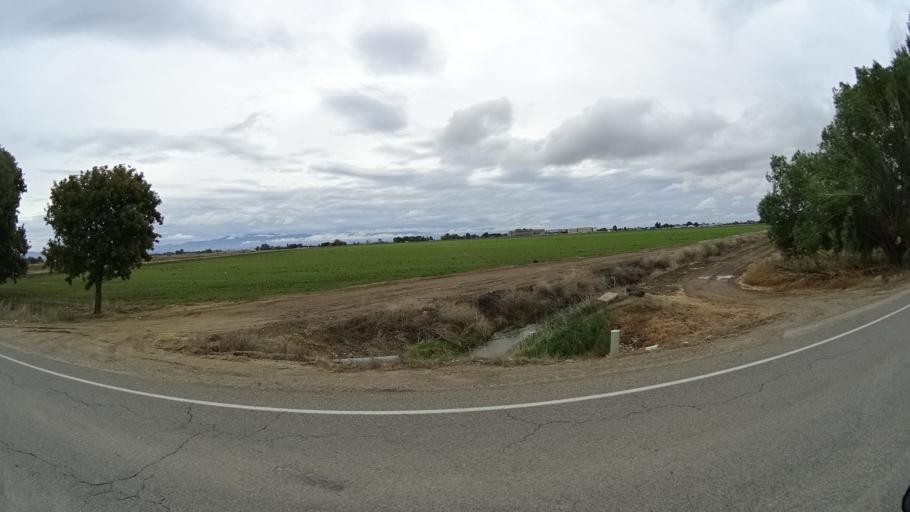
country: US
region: Idaho
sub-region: Ada County
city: Star
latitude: 43.6408
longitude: -116.4936
